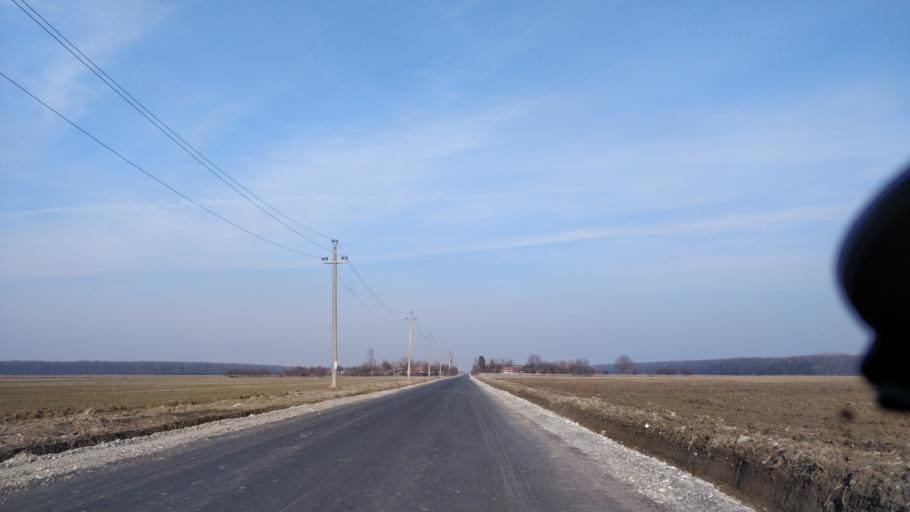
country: RO
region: Giurgiu
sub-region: Comuna Ulmi
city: Trestieni
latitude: 44.5180
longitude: 25.7720
